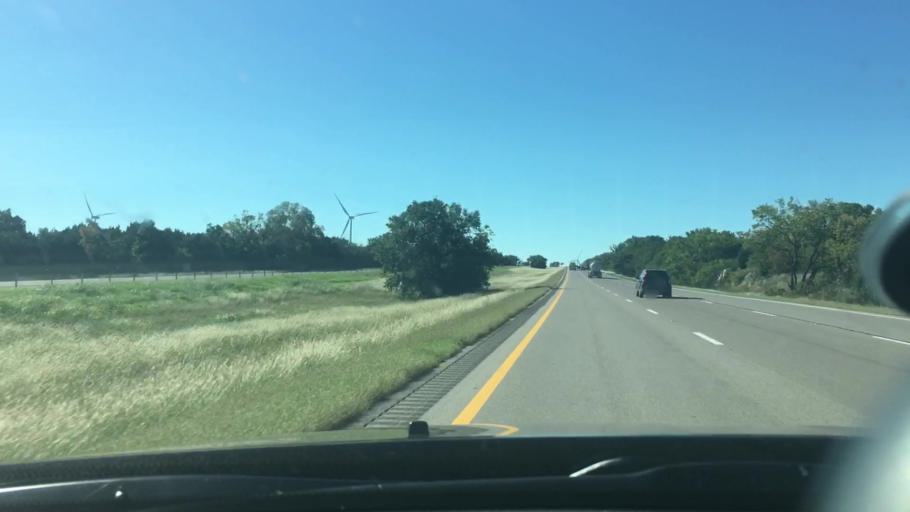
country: US
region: Oklahoma
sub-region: Murray County
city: Davis
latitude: 34.4149
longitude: -97.1381
